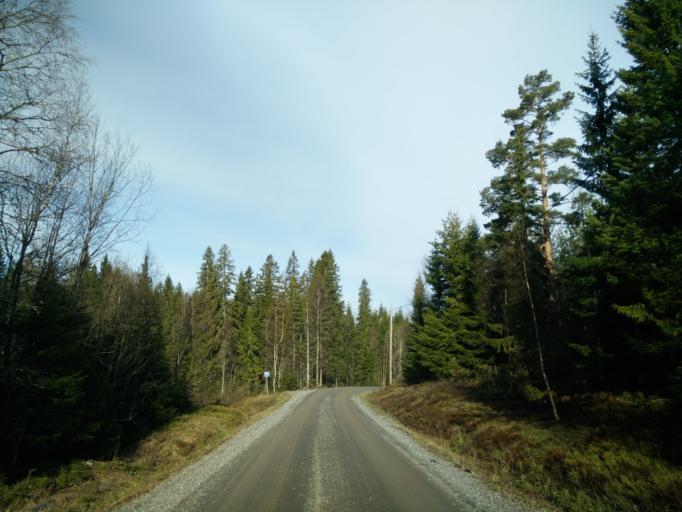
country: SE
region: Vaesternorrland
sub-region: Haernoesands Kommun
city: Haernoesand
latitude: 62.6119
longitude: 17.7139
